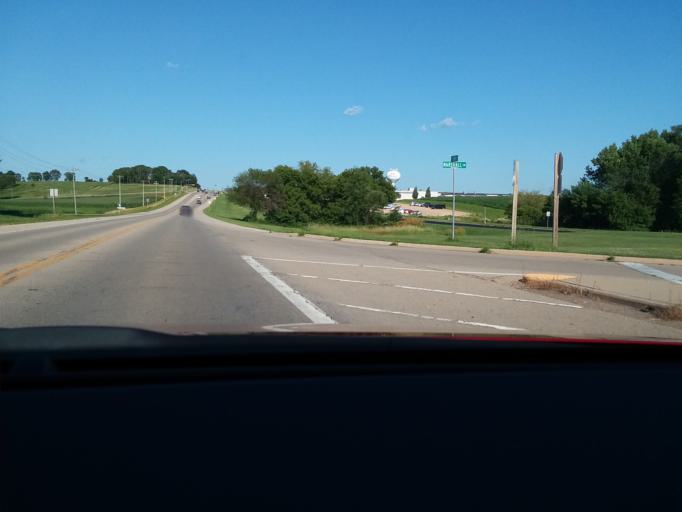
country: US
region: Wisconsin
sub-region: Dane County
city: Waunakee
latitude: 43.1920
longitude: -89.4428
